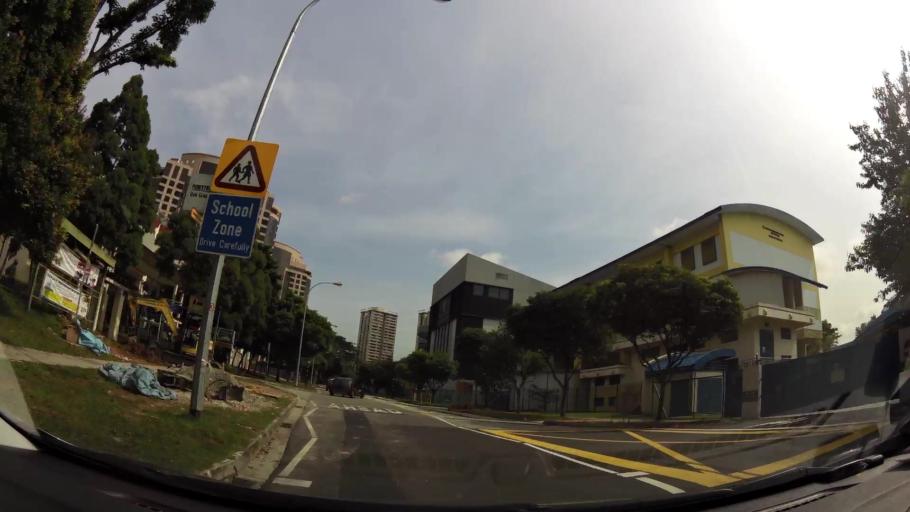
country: SG
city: Singapore
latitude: 1.3023
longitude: 103.7837
